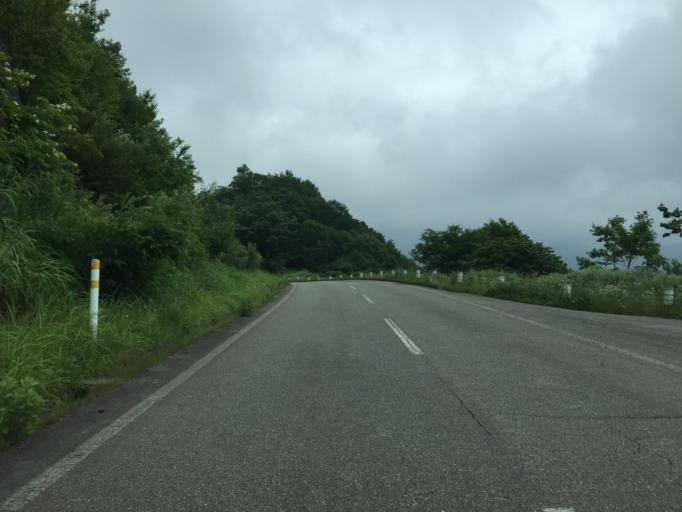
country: JP
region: Fukushima
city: Inawashiro
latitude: 37.6757
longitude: 140.1255
